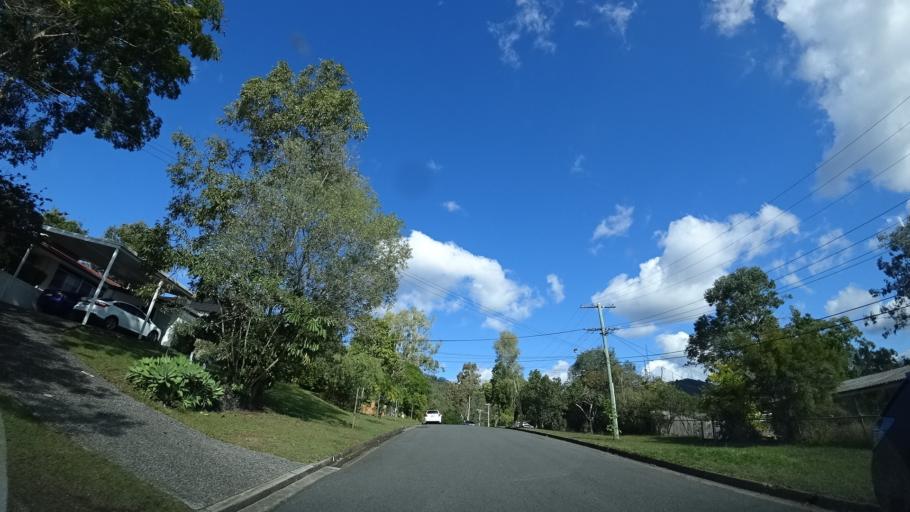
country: AU
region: Queensland
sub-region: Brisbane
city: Taringa
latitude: -27.4491
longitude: 152.9571
